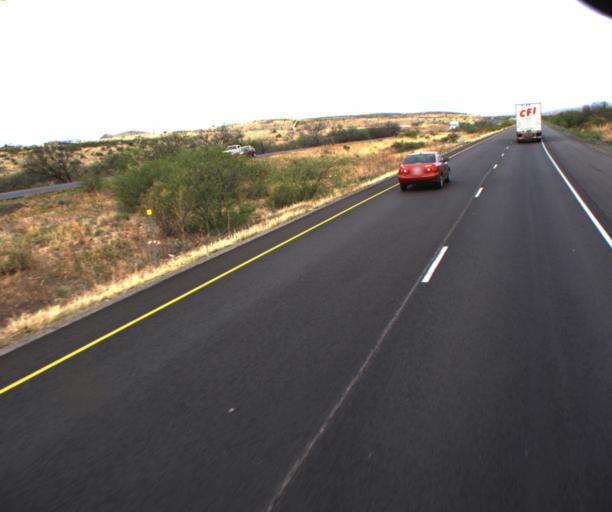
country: US
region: Arizona
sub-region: Cochise County
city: Mescal
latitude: 31.9654
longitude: -110.4595
